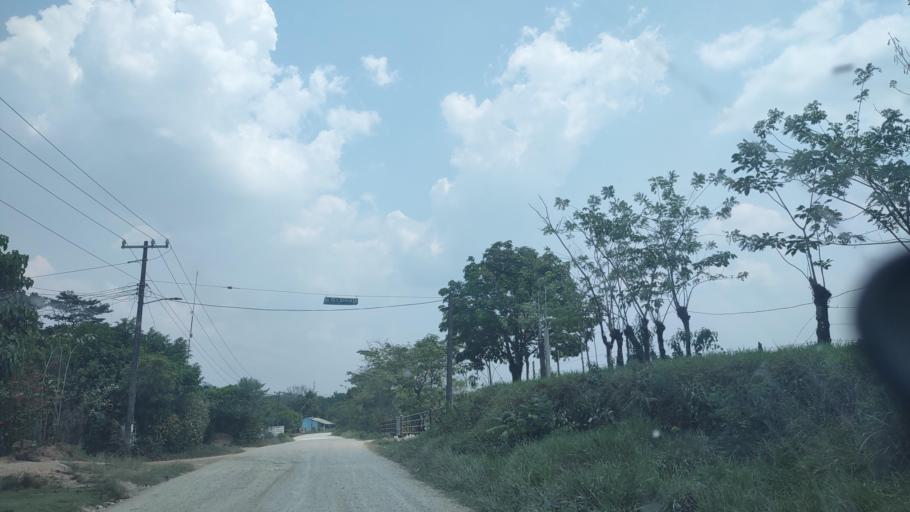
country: MX
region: Tabasco
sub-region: Huimanguillo
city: Francisco Rueda
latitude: 17.6017
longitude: -93.9009
